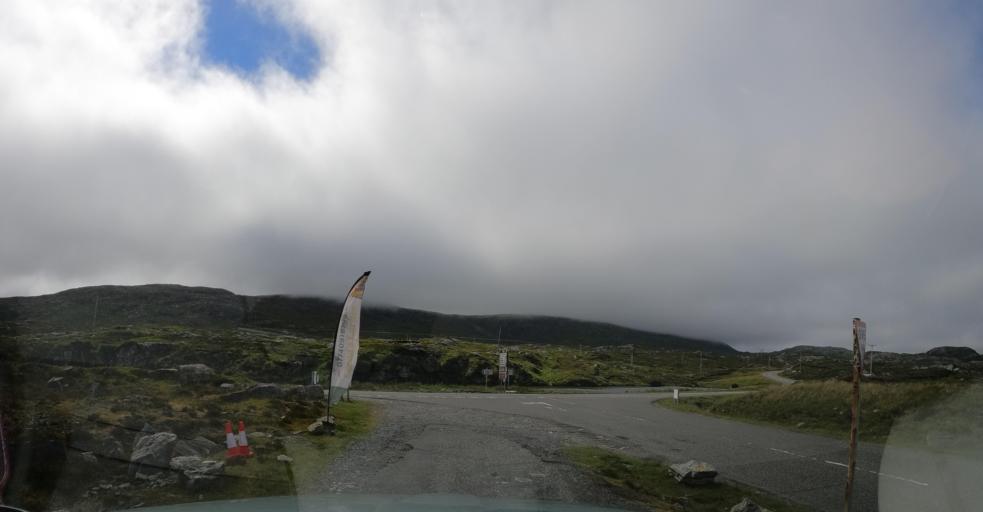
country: GB
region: Scotland
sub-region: Eilean Siar
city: Harris
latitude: 57.8714
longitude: -6.8167
